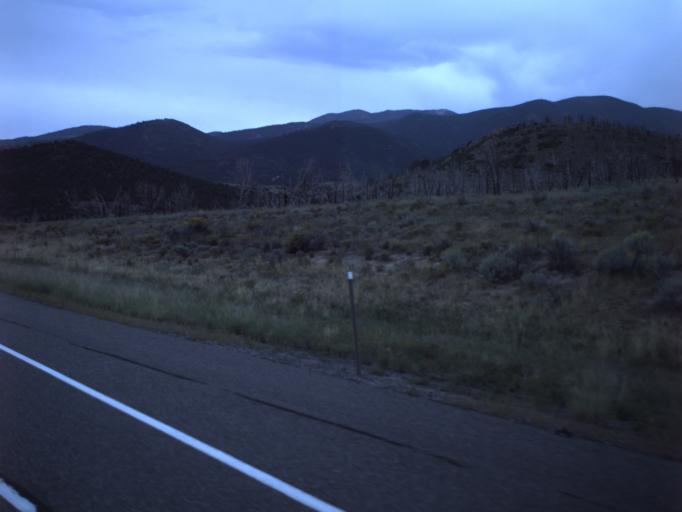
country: US
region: Utah
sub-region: Sevier County
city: Monroe
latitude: 38.5529
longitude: -112.4109
